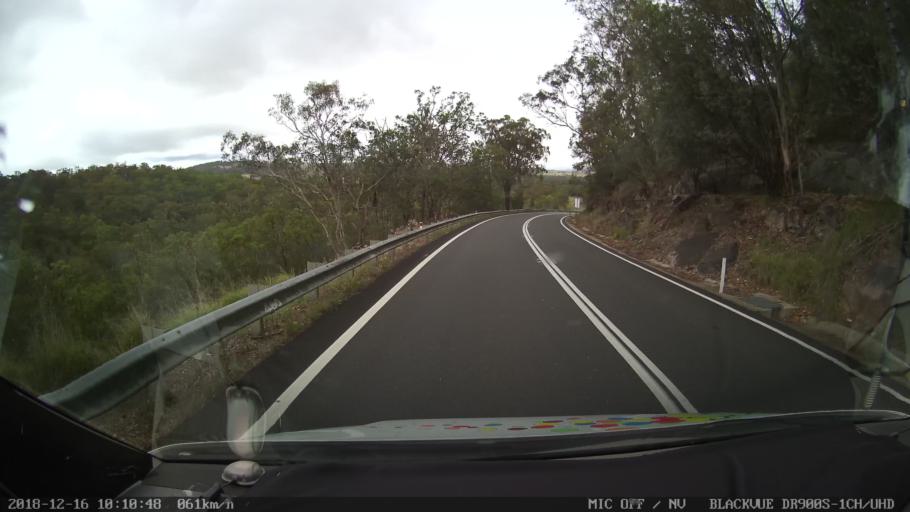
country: AU
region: New South Wales
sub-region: Glen Innes Severn
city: Glen Innes
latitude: -29.3161
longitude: 151.9276
